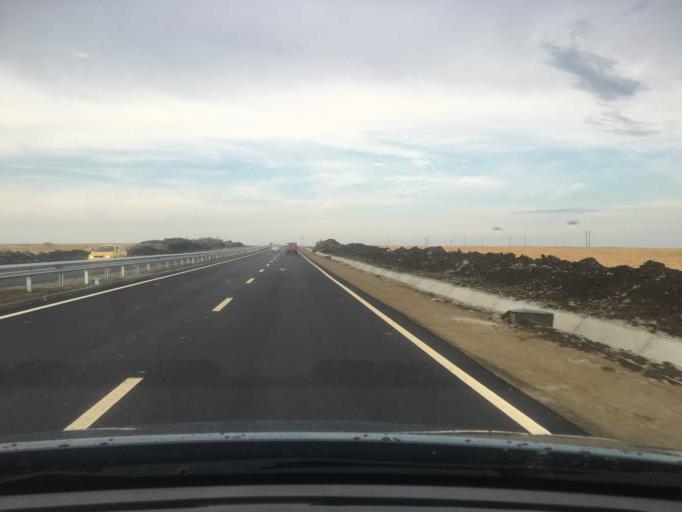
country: BG
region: Burgas
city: Aheloy
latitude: 42.6561
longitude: 27.6503
